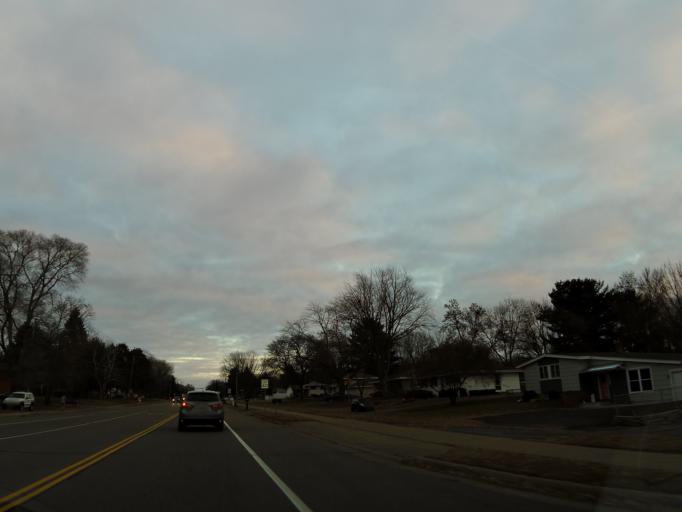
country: US
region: Minnesota
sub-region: Washington County
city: Birchwood
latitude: 45.0502
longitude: -93.0047
